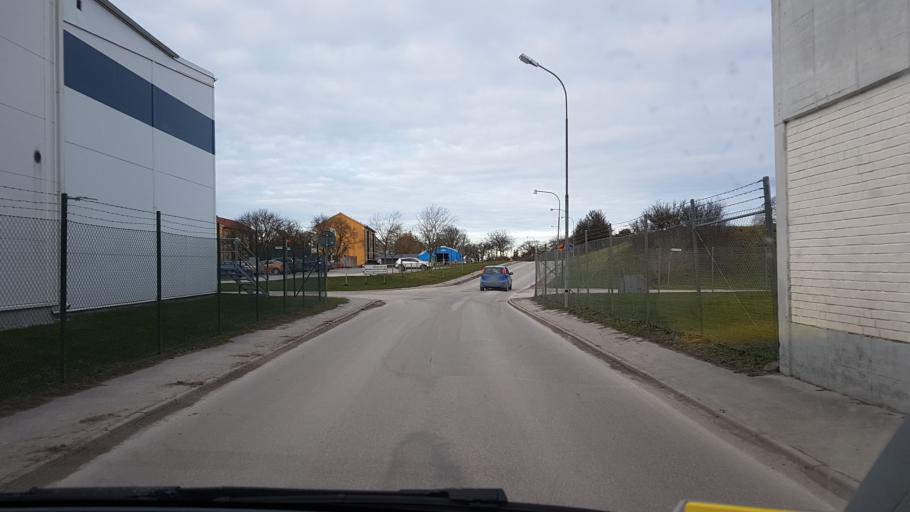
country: SE
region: Gotland
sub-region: Gotland
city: Visby
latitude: 57.6464
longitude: 18.3155
